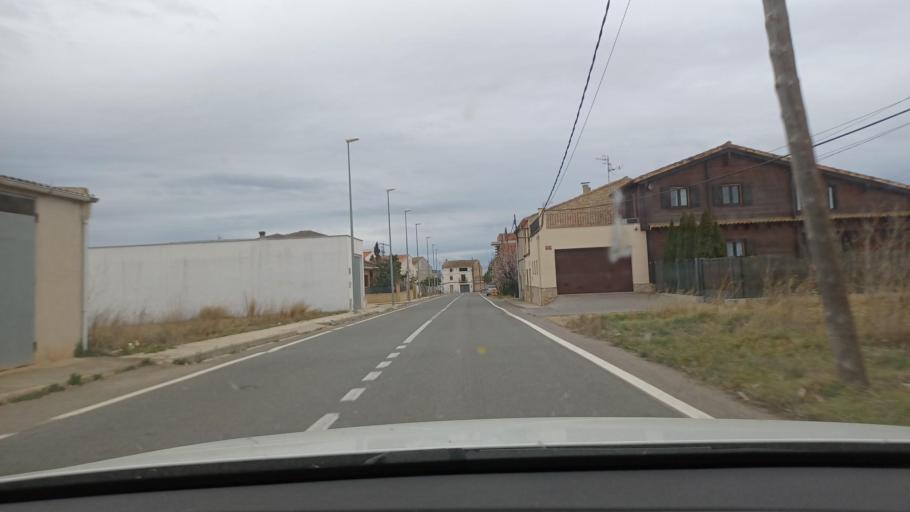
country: ES
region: Catalonia
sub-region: Provincia de Tarragona
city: Ulldecona
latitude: 40.6251
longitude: 0.3655
